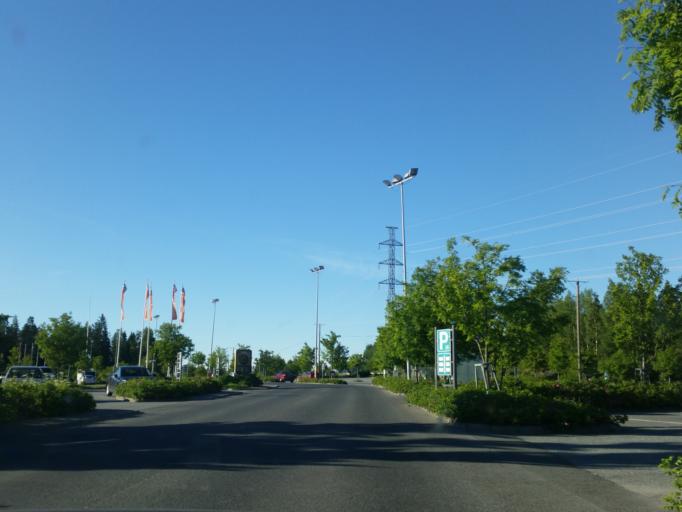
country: FI
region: Northern Savo
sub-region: Kuopio
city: Kuopio
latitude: 62.8632
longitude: 27.6147
